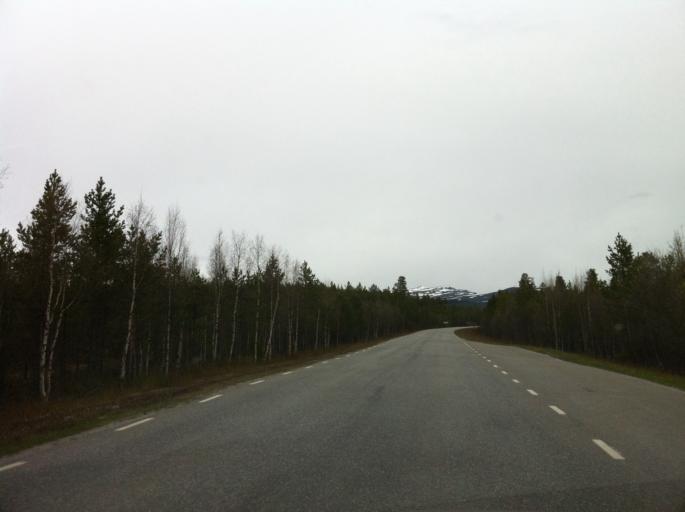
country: NO
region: Hedmark
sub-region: Engerdal
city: Engerdal
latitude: 62.5266
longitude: 12.5793
